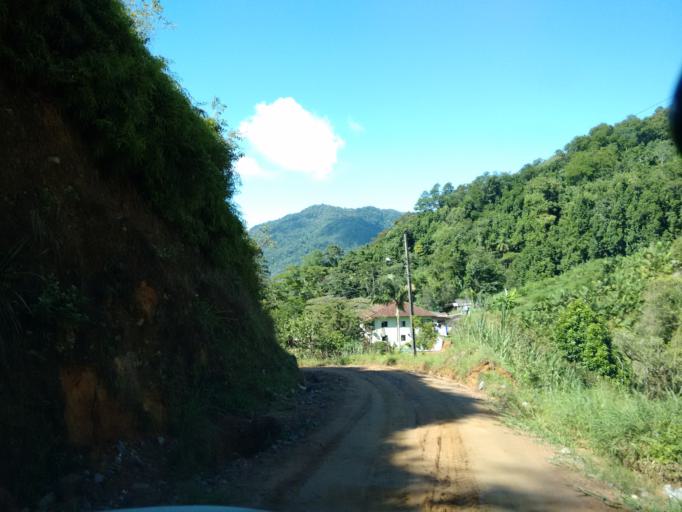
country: BR
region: Santa Catarina
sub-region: Pomerode
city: Pomerode
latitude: -26.7585
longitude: -49.1920
